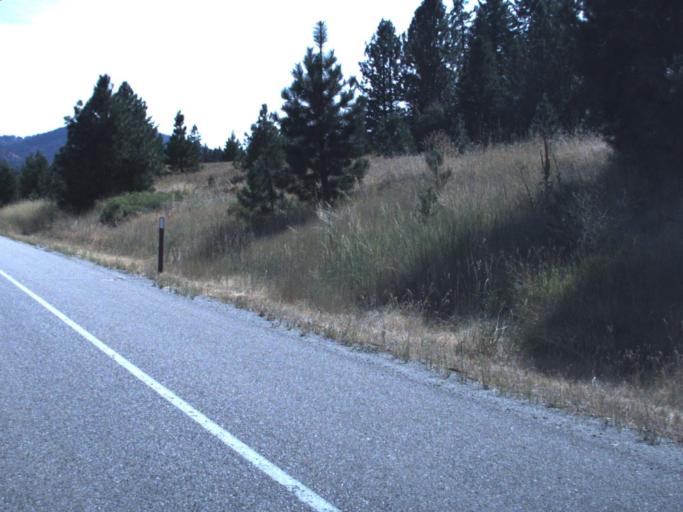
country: US
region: Washington
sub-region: Stevens County
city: Chewelah
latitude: 48.2923
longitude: -117.7380
